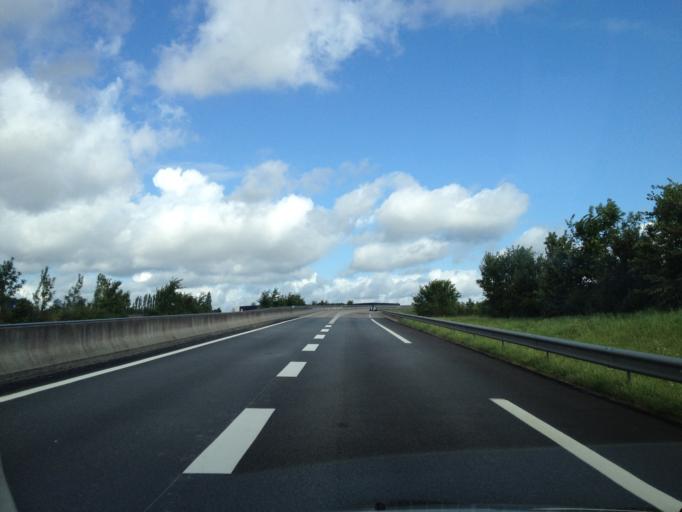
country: FR
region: Haute-Normandie
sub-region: Departement de l'Eure
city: Bourg-Achard
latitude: 49.3611
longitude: 0.8324
